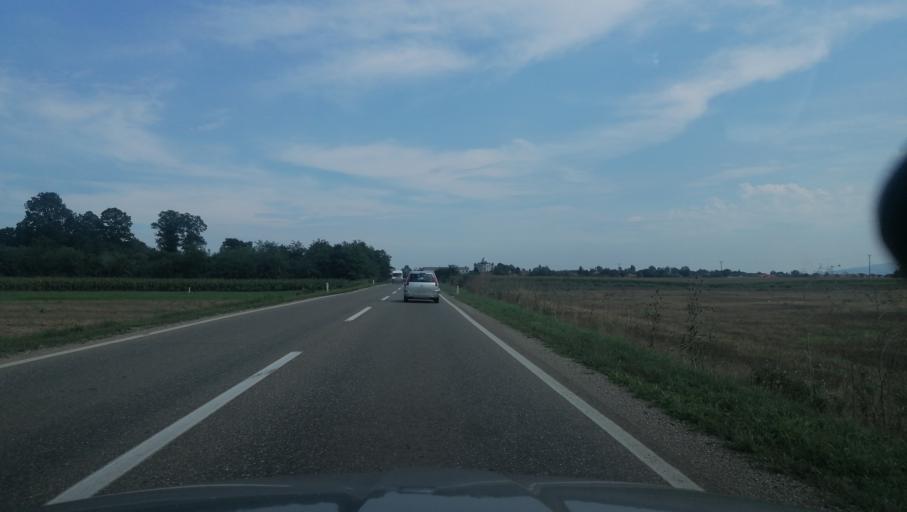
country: BA
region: Republika Srpska
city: Dvorovi
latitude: 44.7869
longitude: 19.2636
